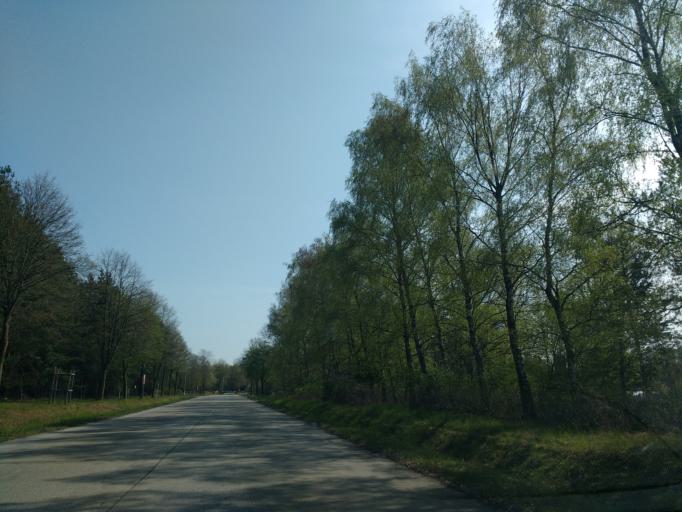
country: DE
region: North Rhine-Westphalia
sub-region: Regierungsbezirk Detmold
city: Hovelhof
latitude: 51.8237
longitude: 8.7182
